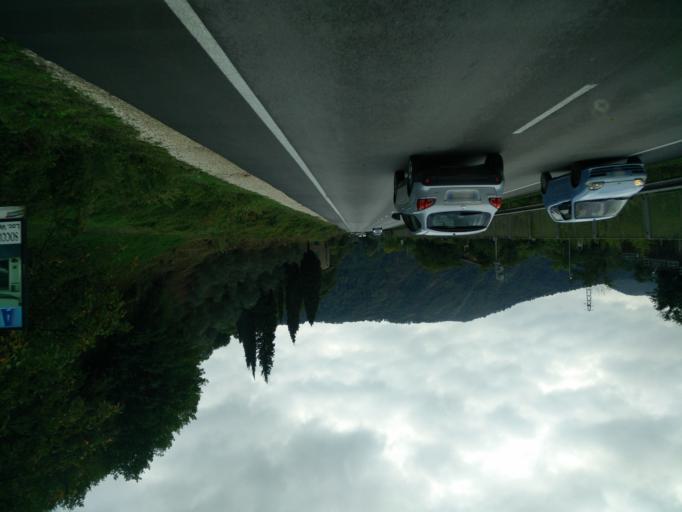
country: IT
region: Tuscany
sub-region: Provincia di Lucca
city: Valdottavo
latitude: 43.9491
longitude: 10.4989
